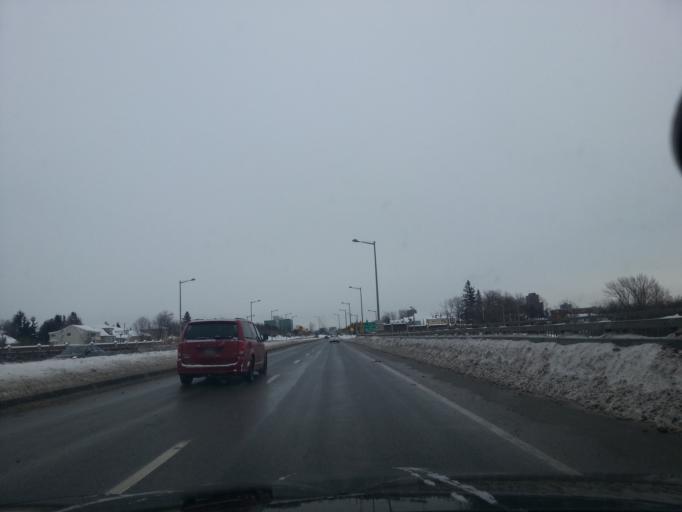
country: CA
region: Ontario
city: Ottawa
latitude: 45.4323
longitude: -75.7458
